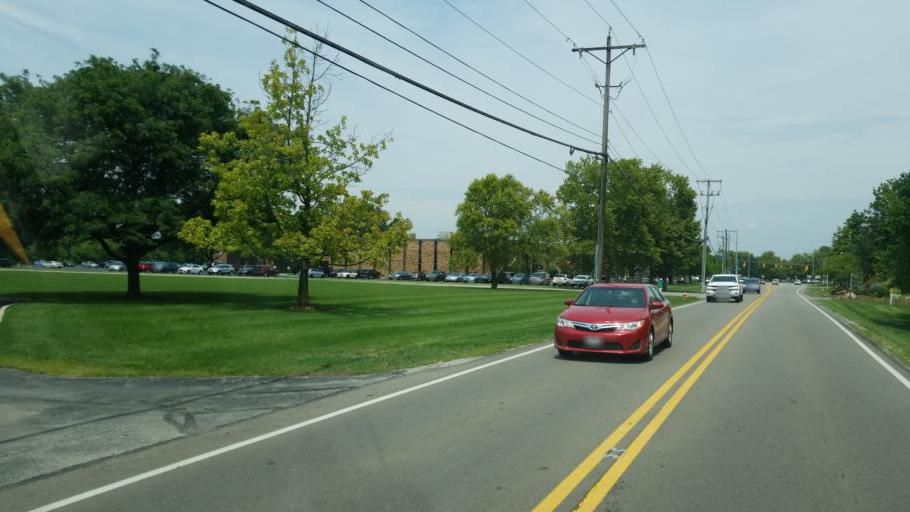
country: US
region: Ohio
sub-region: Franklin County
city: Worthington
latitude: 40.0614
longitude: -83.0666
